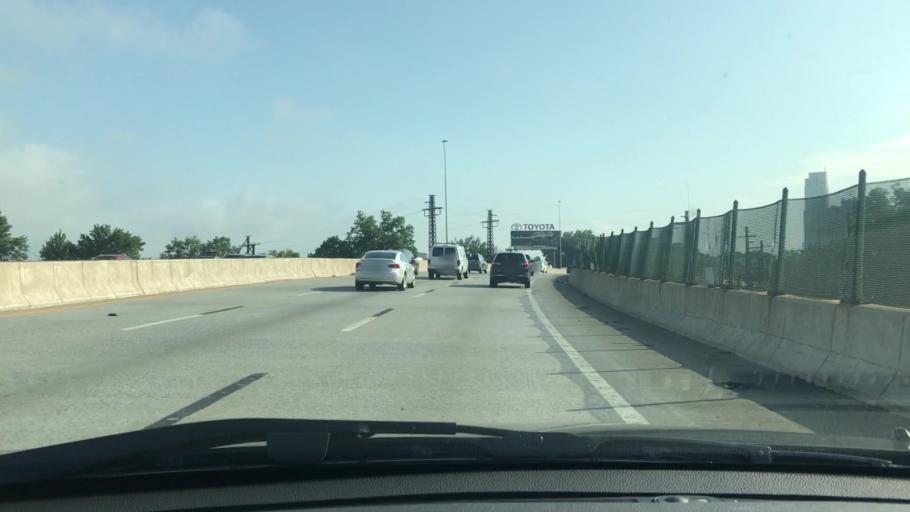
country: US
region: New York
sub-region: Westchester County
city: New Rochelle
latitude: 40.9059
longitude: -73.7914
